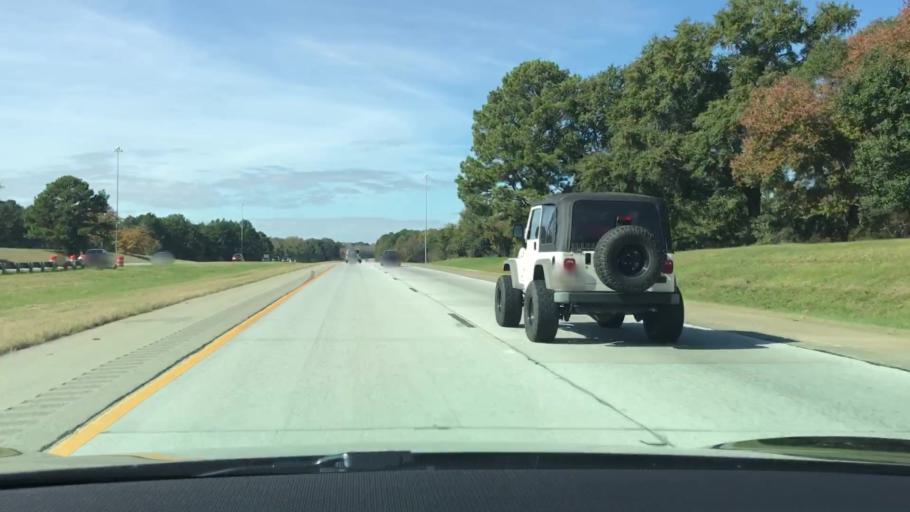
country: US
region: Georgia
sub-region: Morgan County
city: Madison
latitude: 33.5554
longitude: -83.4751
